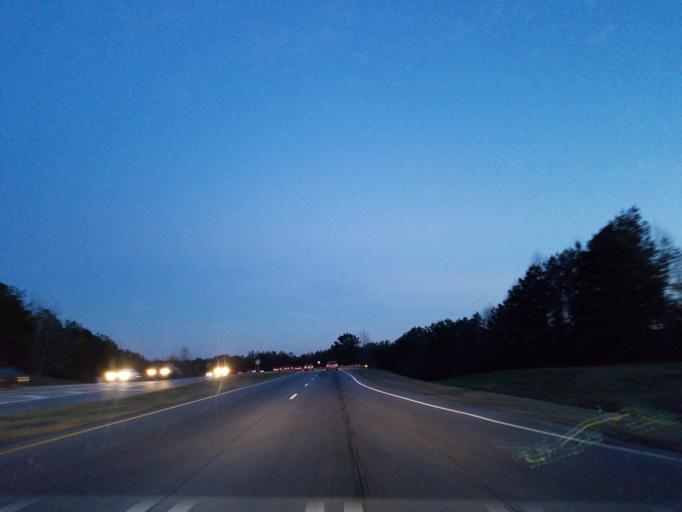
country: US
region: Georgia
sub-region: Paulding County
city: Dallas
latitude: 33.9029
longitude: -84.8101
